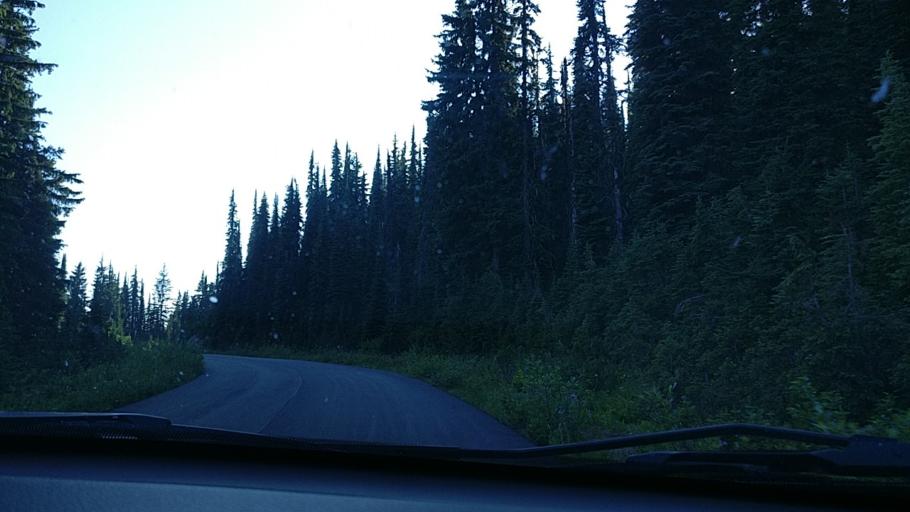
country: CA
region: British Columbia
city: Revelstoke
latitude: 51.0264
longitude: -118.1611
